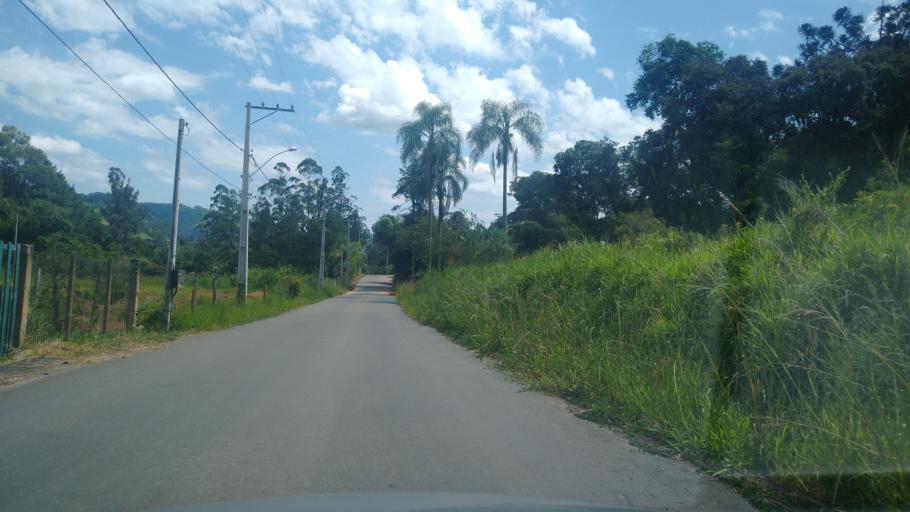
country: BR
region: Minas Gerais
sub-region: Extrema
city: Extrema
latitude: -22.7931
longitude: -46.2885
